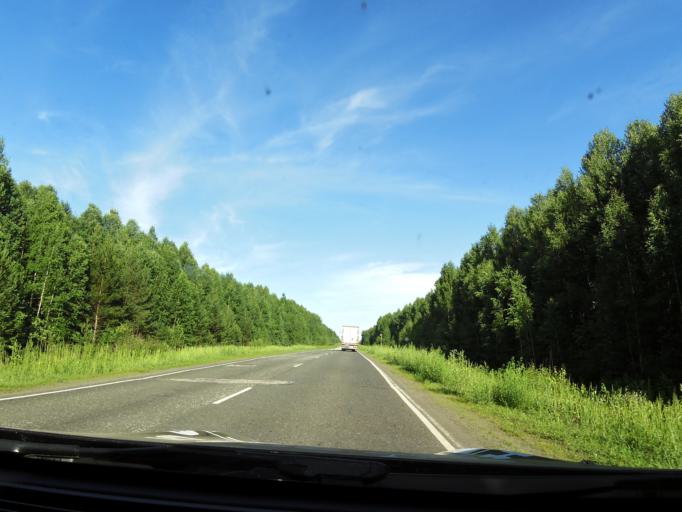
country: RU
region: Kirov
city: Chernaya Kholunitsa
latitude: 58.8827
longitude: 51.4207
